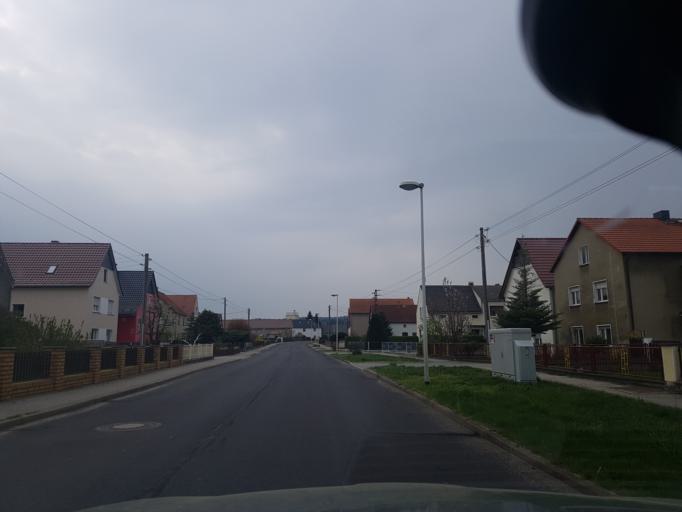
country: DE
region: Brandenburg
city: Grosskmehlen
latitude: 51.3856
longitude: 13.7116
